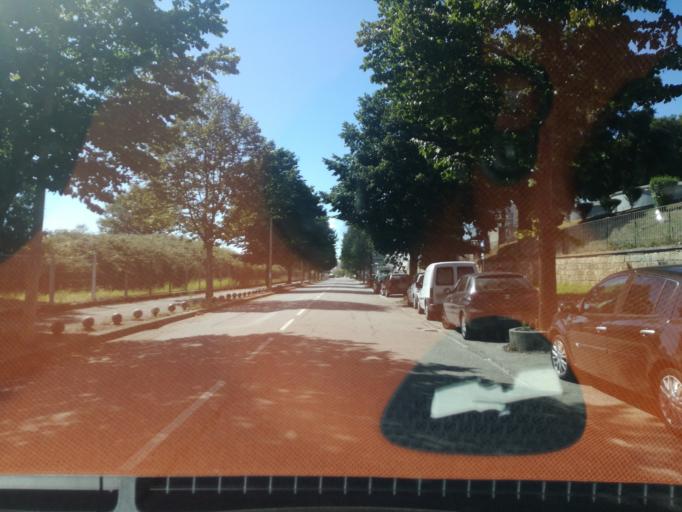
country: PT
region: Porto
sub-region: Matosinhos
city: Sao Mamede de Infesta
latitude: 41.1794
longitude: -8.6023
